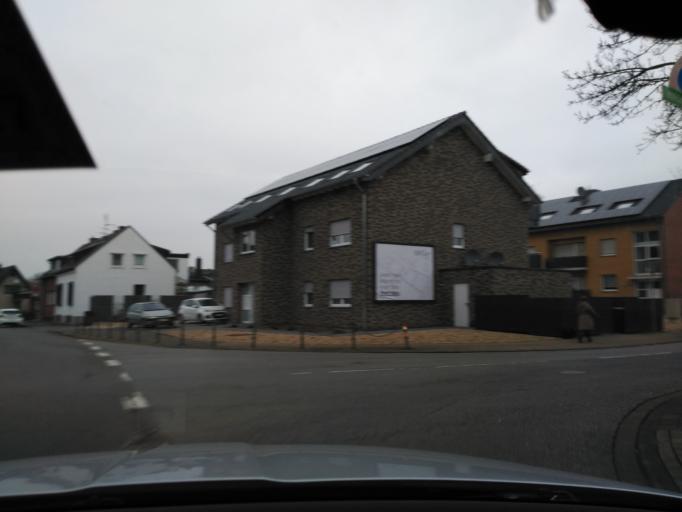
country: DE
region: North Rhine-Westphalia
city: Wegberg
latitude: 51.1380
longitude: 6.2773
